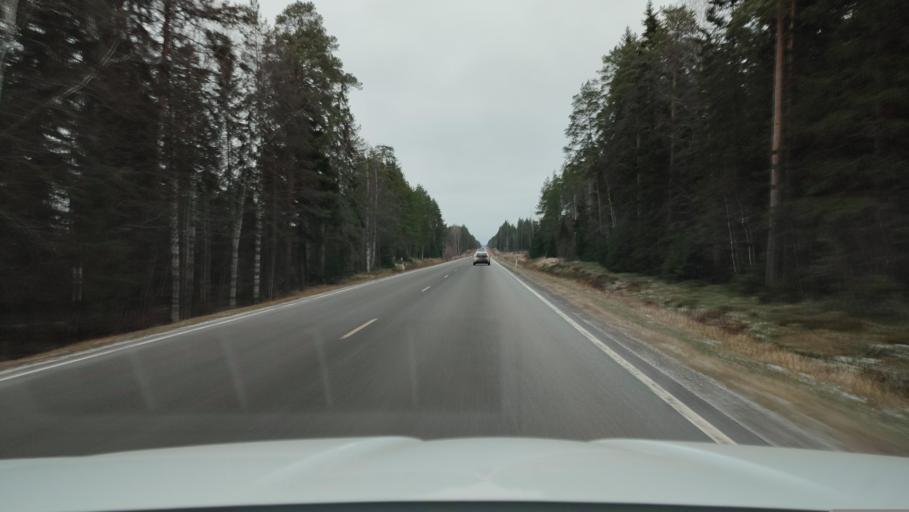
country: FI
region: Ostrobothnia
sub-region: Sydosterbotten
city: Naerpes
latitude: 62.5814
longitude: 21.4943
